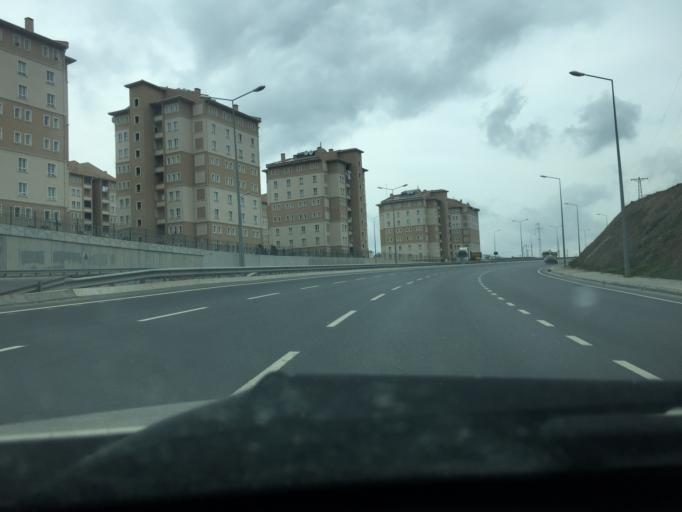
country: TR
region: Istanbul
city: Basaksehir
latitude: 41.1357
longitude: 28.7911
